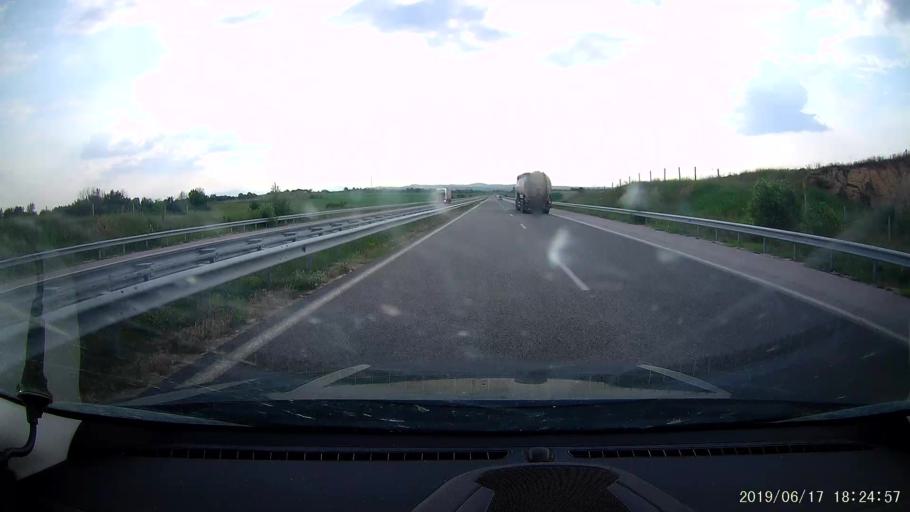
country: BG
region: Khaskovo
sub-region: Obshtina Dimitrovgrad
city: Dimitrovgrad
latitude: 41.9889
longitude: 25.6752
